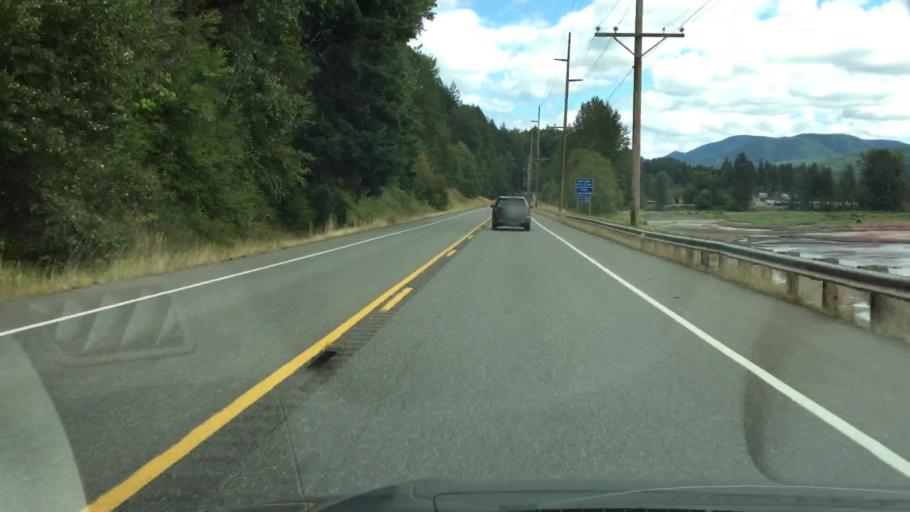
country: US
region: Washington
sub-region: Pierce County
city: Eatonville
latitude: 46.7696
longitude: -122.2045
